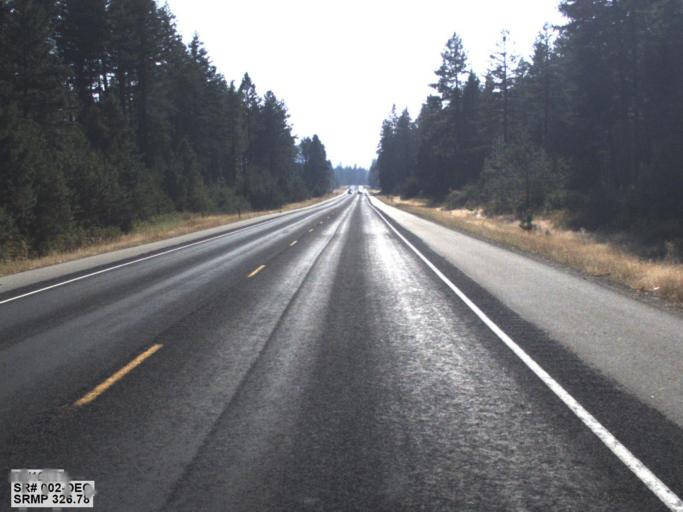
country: US
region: Washington
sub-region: Pend Oreille County
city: Newport
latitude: 48.1317
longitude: -117.1769
